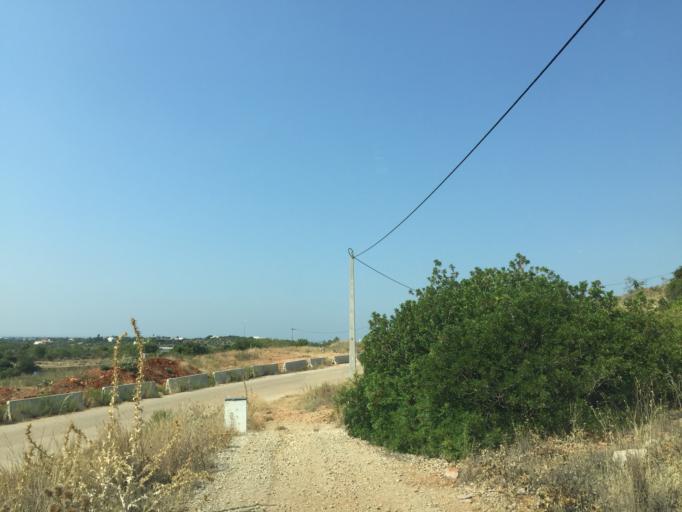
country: PT
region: Faro
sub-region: Loule
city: Almancil
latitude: 37.1009
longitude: -8.0060
